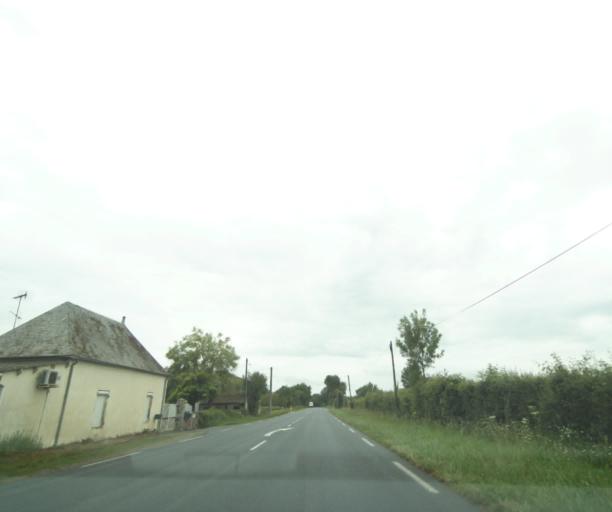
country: FR
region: Poitou-Charentes
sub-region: Departement des Deux-Sevres
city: Viennay
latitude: 46.7070
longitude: -0.2392
